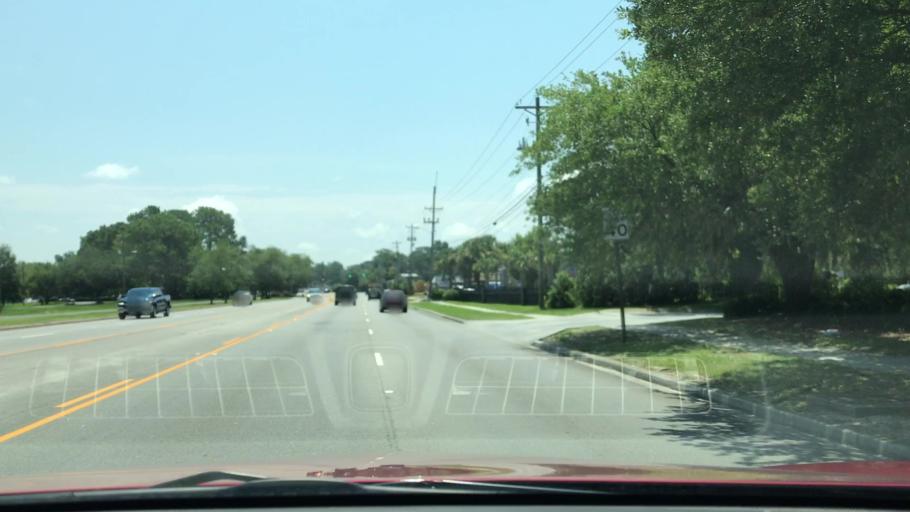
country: US
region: South Carolina
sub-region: Berkeley County
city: Hanahan
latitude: 32.8593
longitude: -80.0455
